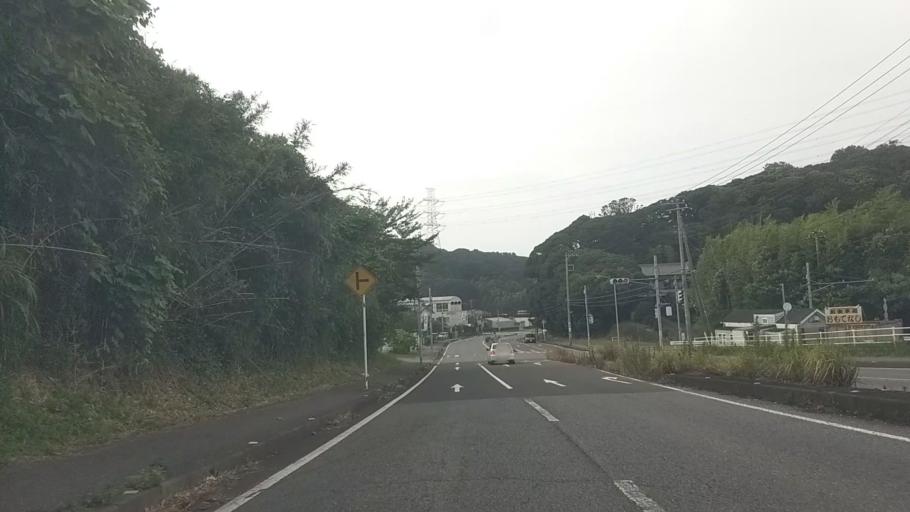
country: JP
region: Chiba
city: Kimitsu
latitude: 35.3416
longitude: 139.8914
